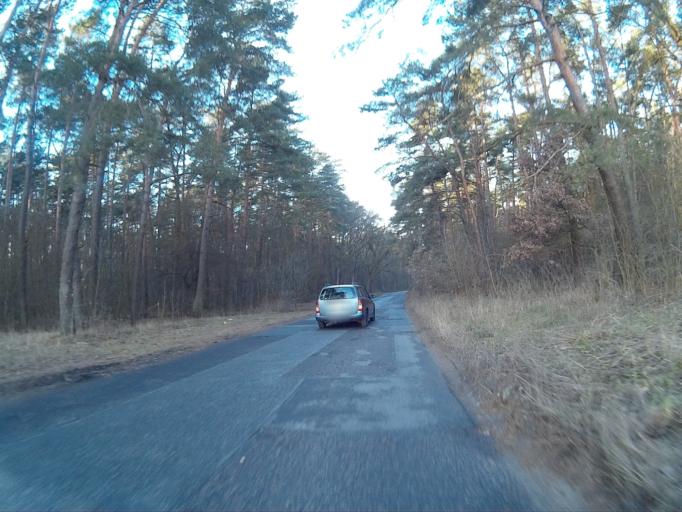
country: PL
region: Kujawsko-Pomorskie
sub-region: Powiat bydgoski
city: Osielsko
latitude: 53.1603
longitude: 18.0692
